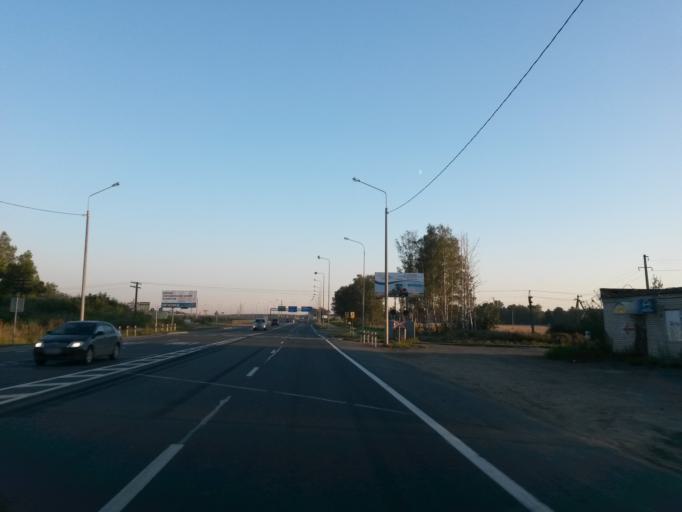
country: RU
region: Jaroslavl
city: Yaroslavl
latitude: 57.6948
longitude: 39.8986
